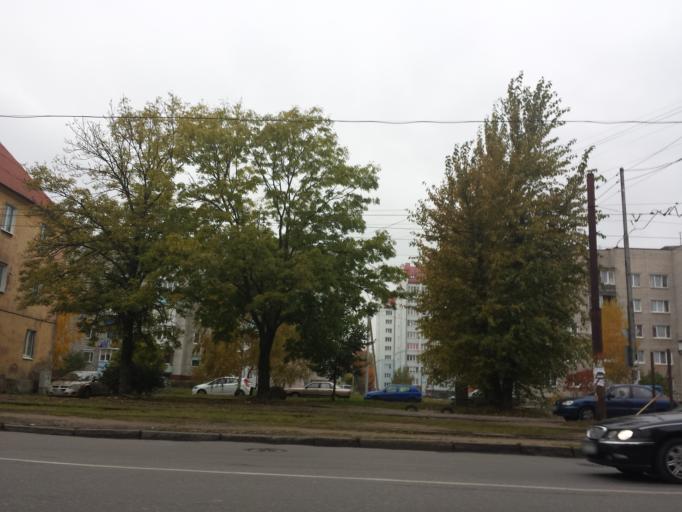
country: RU
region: Kaliningrad
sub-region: Gorod Kaliningrad
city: Kaliningrad
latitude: 54.6910
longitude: 20.5237
